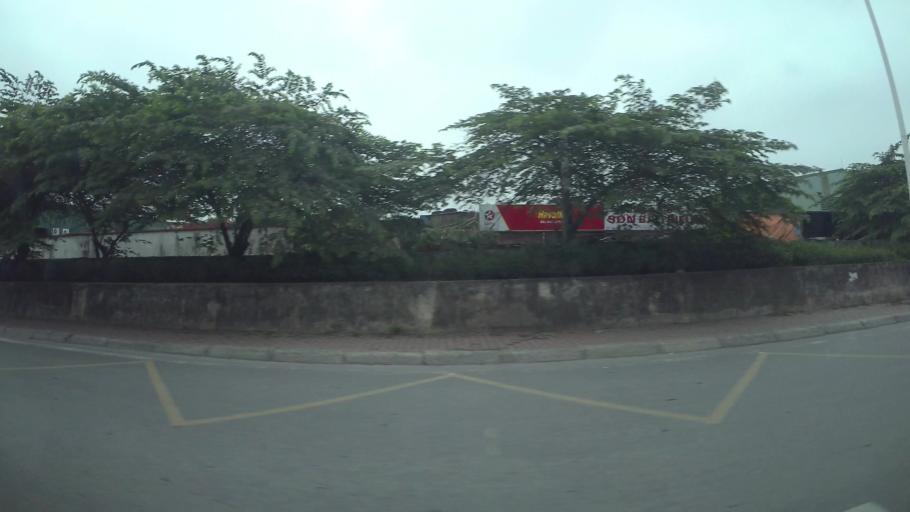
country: VN
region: Ha Noi
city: Hai BaTrung
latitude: 21.0044
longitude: 105.8702
